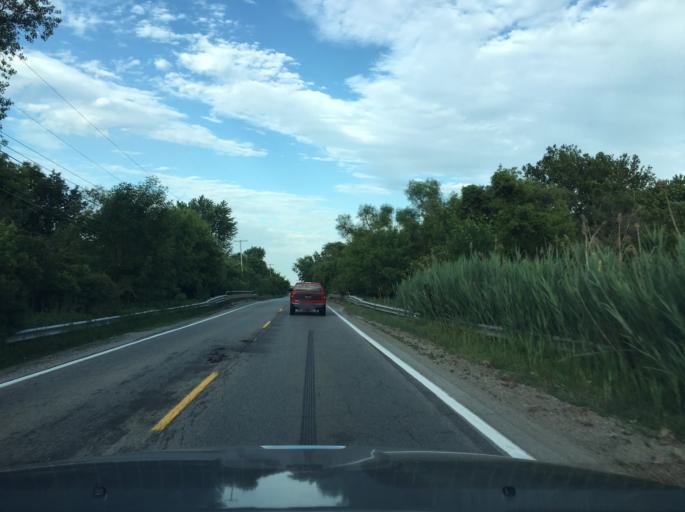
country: US
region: Michigan
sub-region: Macomb County
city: New Haven
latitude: 42.7172
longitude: -82.9053
